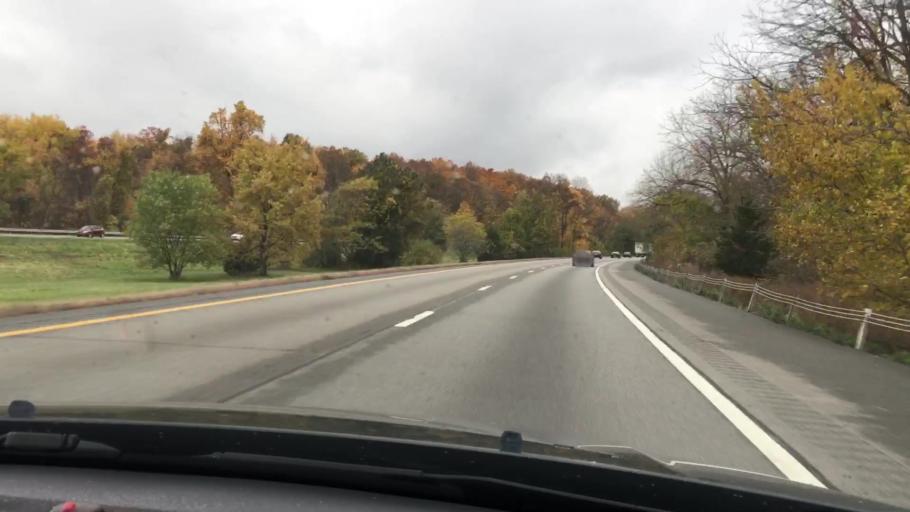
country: US
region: New York
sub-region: Dutchess County
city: Brinckerhoff
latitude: 41.5251
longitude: -73.8609
